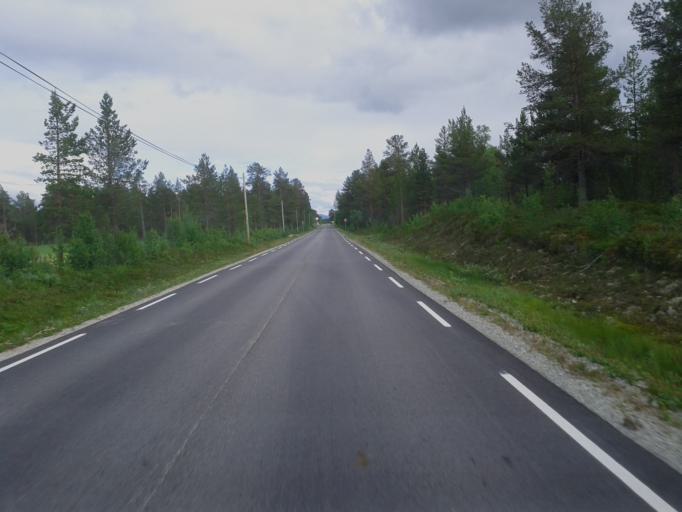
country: NO
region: Sor-Trondelag
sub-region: Roros
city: Roros
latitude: 62.2907
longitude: 11.7311
